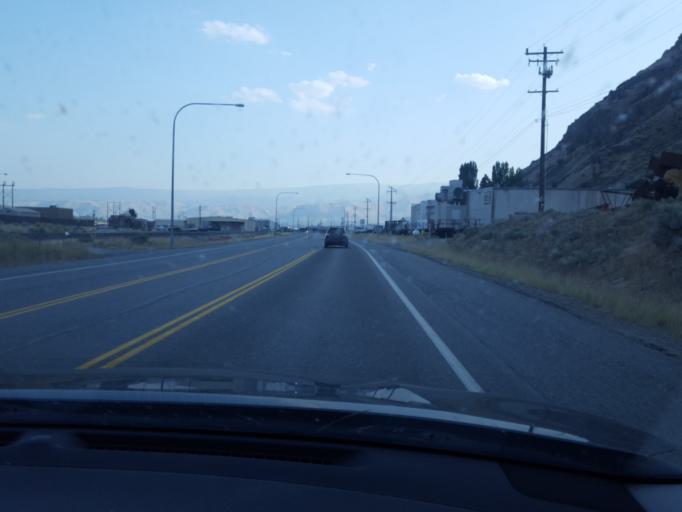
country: US
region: Washington
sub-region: Chelan County
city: Sunnyslope
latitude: 47.4952
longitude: -120.3134
